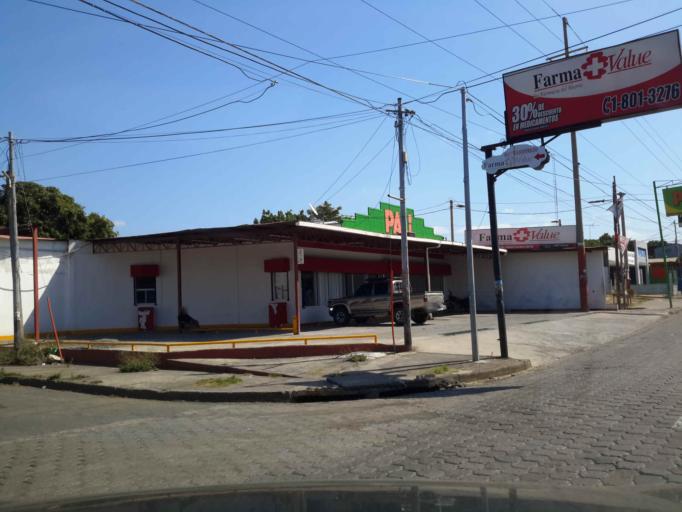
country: NI
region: Managua
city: Ciudad Sandino
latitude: 12.1482
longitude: -86.3047
